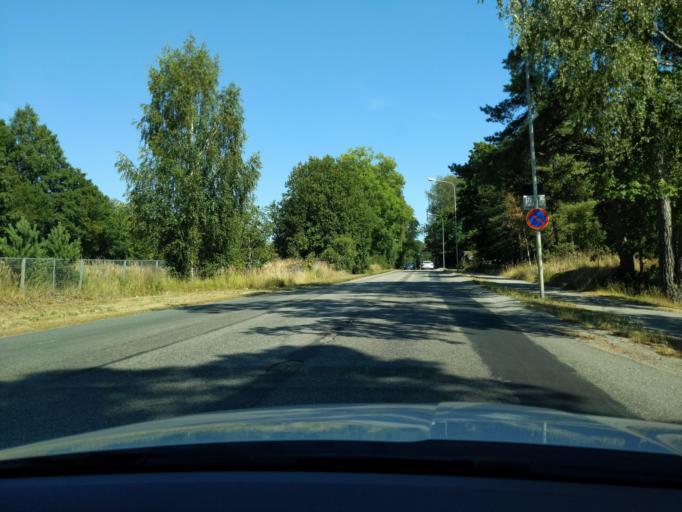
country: FI
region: Uusimaa
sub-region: Raaseporin
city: Hanko
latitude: 59.8276
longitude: 22.9764
